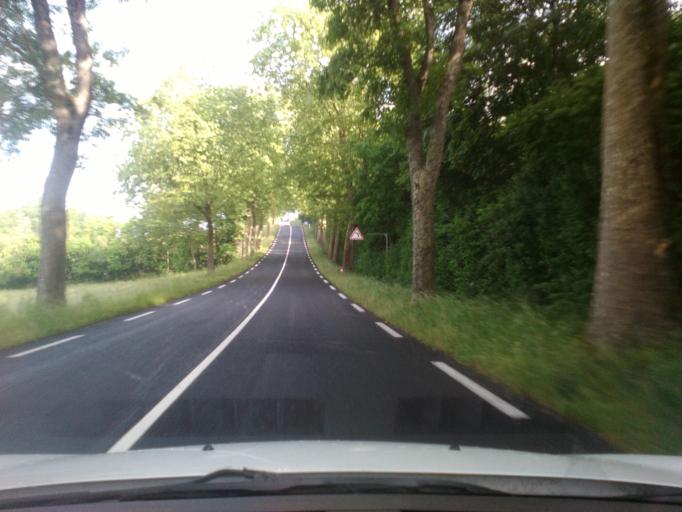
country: FR
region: Lorraine
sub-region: Departement de Meurthe-et-Moselle
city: Gerbeviller
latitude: 48.5152
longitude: 6.4898
